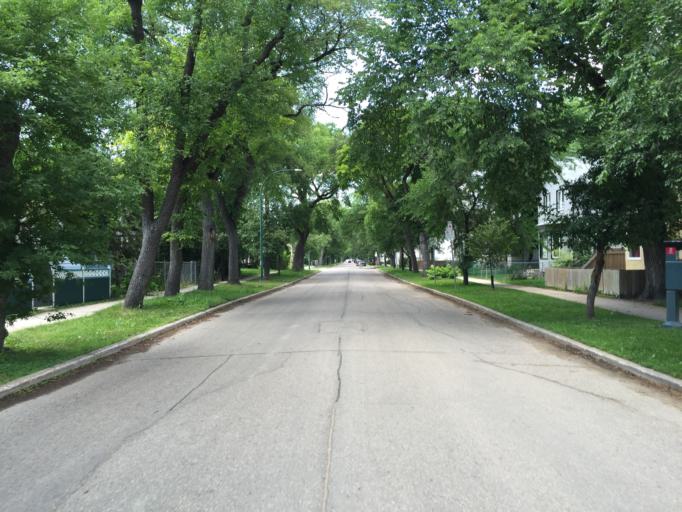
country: CA
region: Manitoba
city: Winnipeg
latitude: 49.9013
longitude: -97.1433
